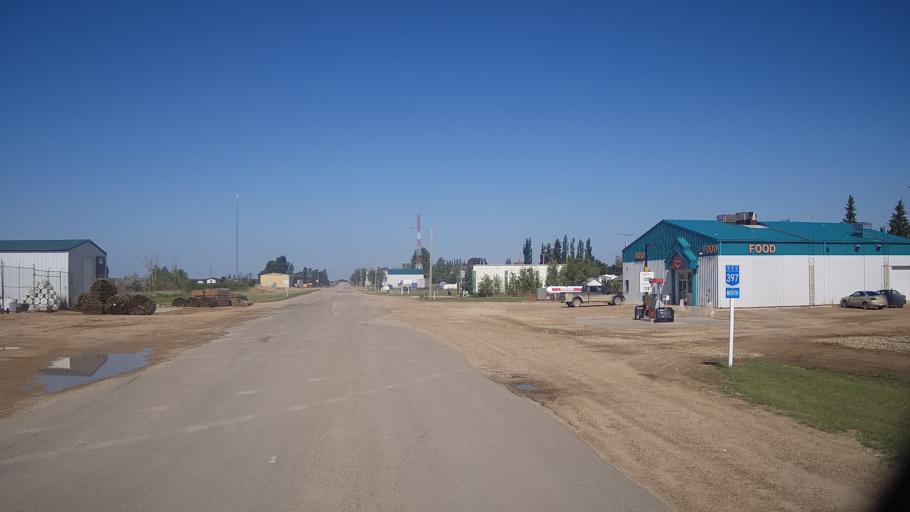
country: CA
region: Saskatchewan
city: Saskatoon
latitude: 51.8914
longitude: -106.0516
